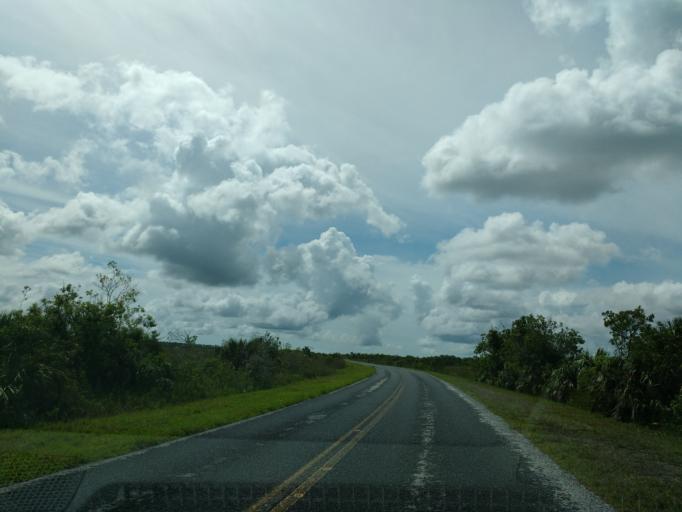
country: US
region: Florida
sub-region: Miami-Dade County
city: Florida City
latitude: 25.3905
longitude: -80.6160
